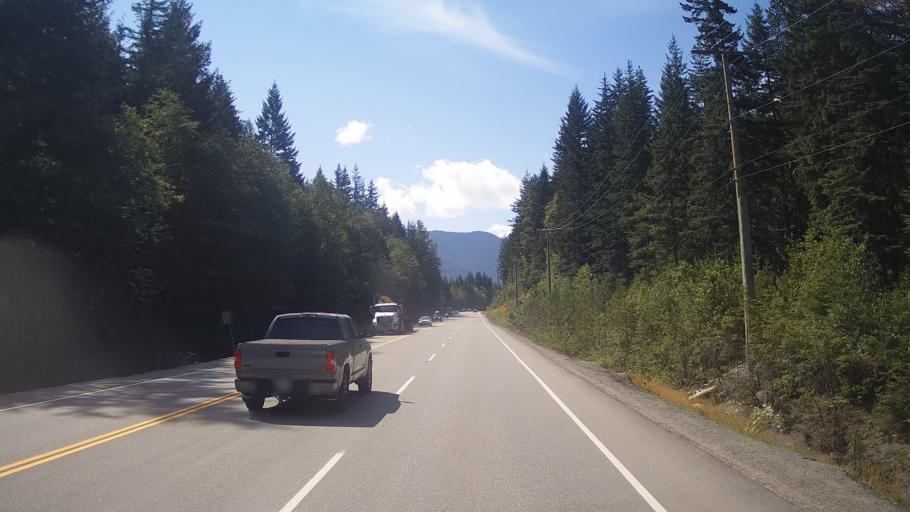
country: CA
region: British Columbia
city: Whistler
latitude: 50.2044
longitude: -122.8818
